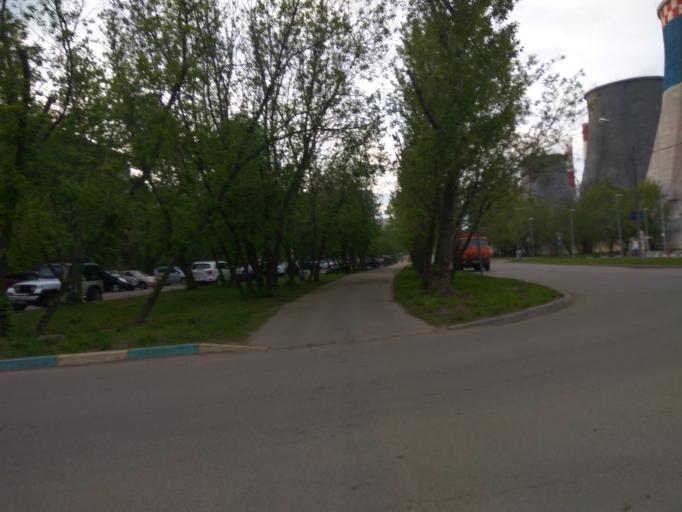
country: RU
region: Moscow
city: Sokol
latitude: 55.7784
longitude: 37.5017
